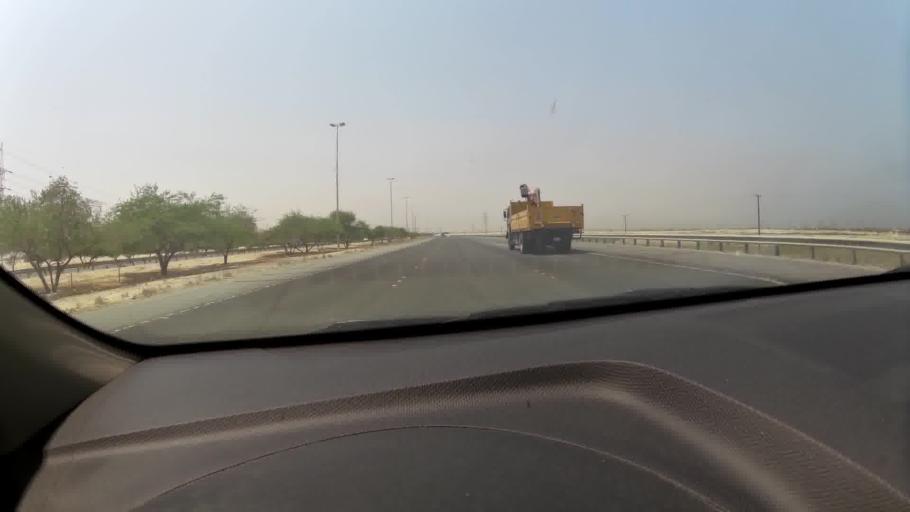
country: KW
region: Al Ahmadi
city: Al Fahahil
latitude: 28.9256
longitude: 48.1965
